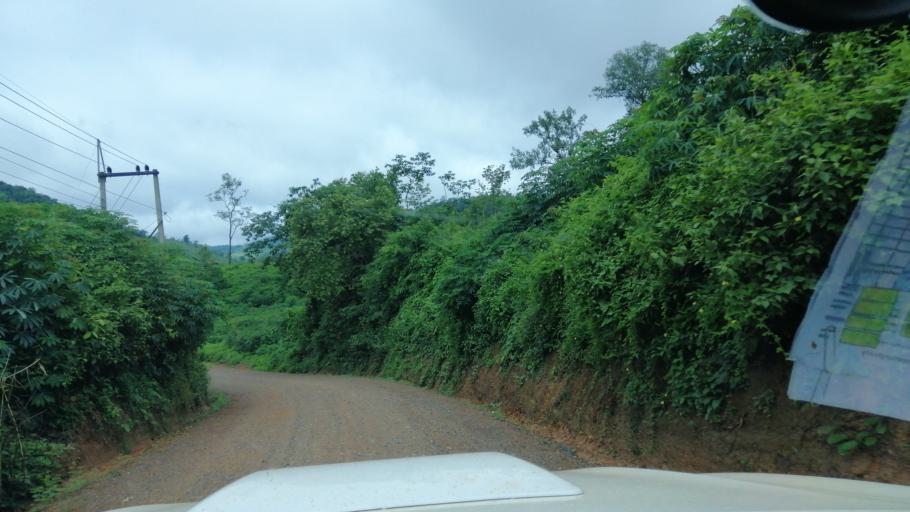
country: LA
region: Xiagnabouli
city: Muang Kenthao
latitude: 17.9183
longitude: 101.3773
